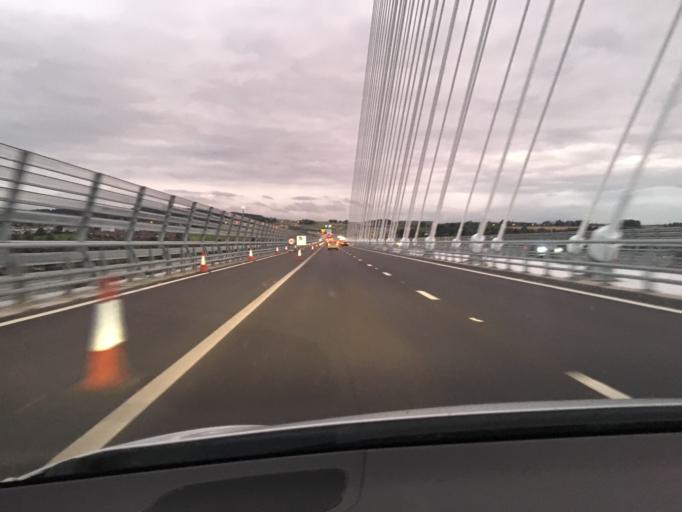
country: GB
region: Scotland
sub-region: Edinburgh
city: Queensferry
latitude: 55.9987
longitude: -3.4160
